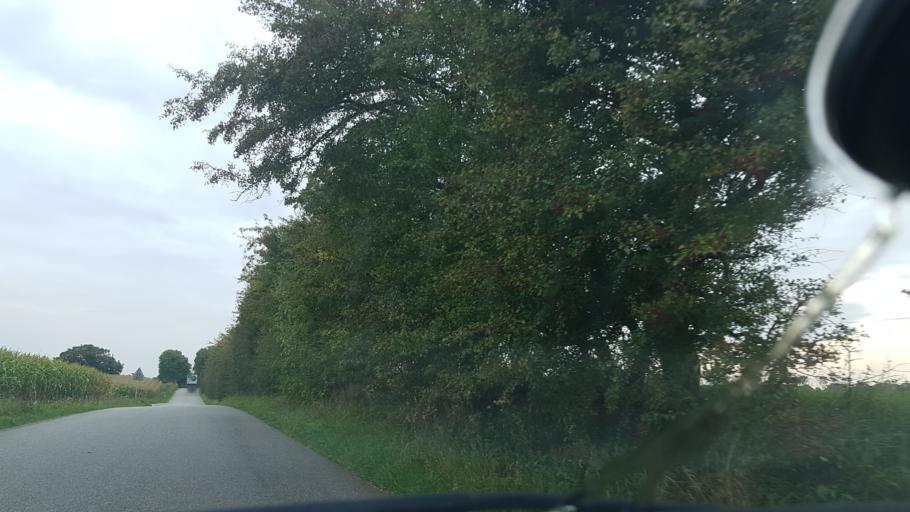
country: DK
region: South Denmark
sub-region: Vejle Kommune
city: Egtved
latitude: 55.5691
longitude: 9.2390
